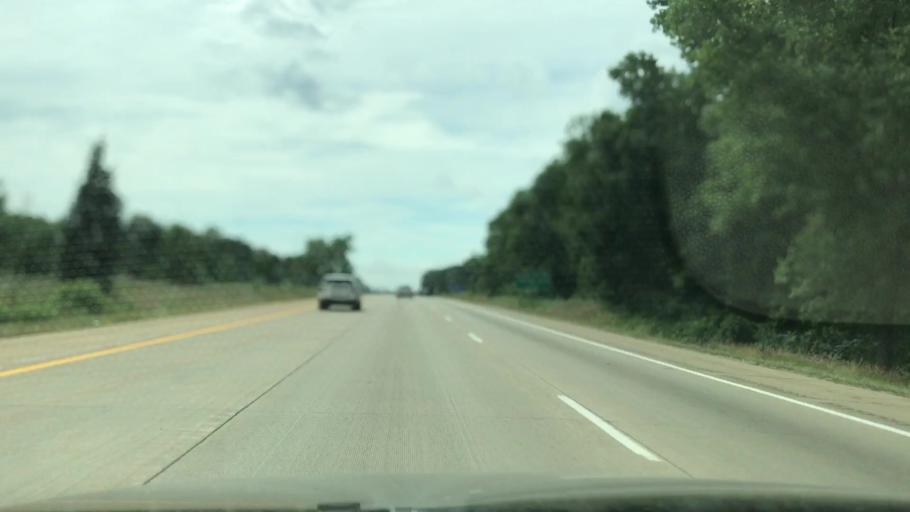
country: US
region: Michigan
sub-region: Kent County
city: Comstock Park
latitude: 43.0191
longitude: -85.7003
